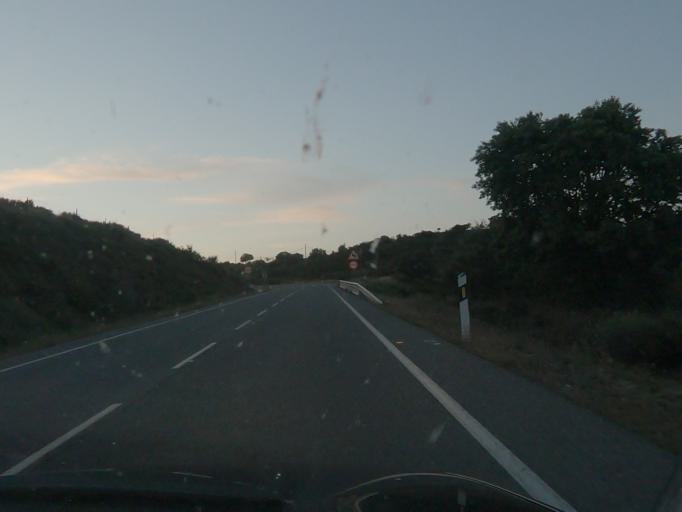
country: ES
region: Extremadura
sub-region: Provincia de Caceres
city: Alcantara
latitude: 39.7320
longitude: -6.9028
